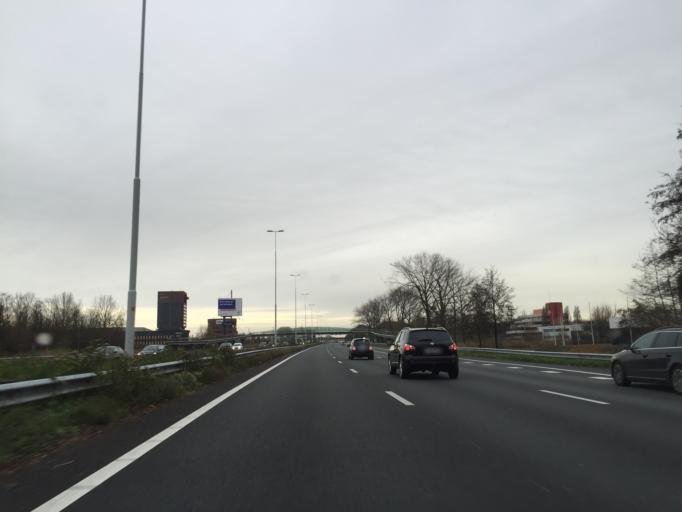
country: NL
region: South Holland
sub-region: Gemeente Dordrecht
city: Dordrecht
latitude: 51.7797
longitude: 4.6504
